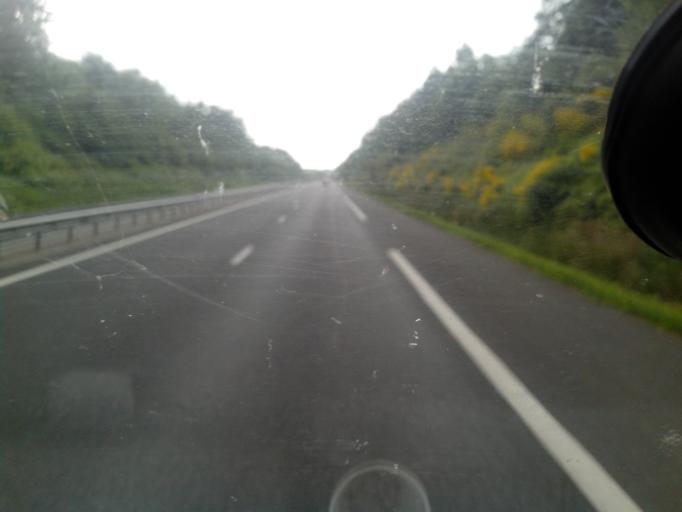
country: FR
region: Lower Normandy
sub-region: Departement du Calvados
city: Saint-Gatien-des-Bois
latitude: 49.3391
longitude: 0.2422
